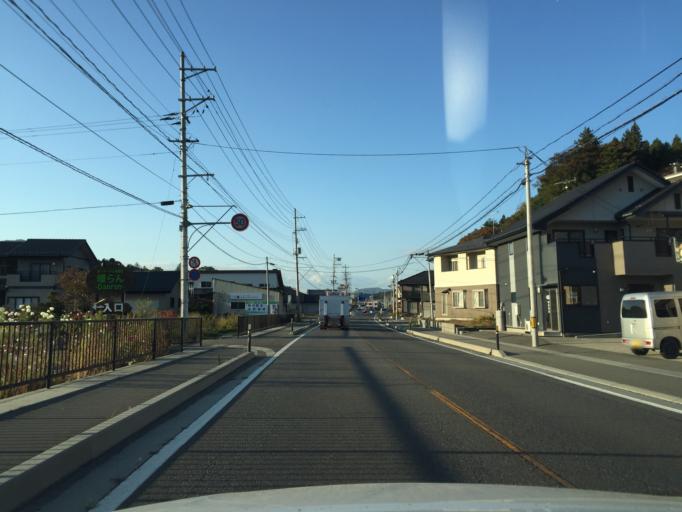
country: JP
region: Fukushima
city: Ishikawa
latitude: 37.2377
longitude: 140.5705
